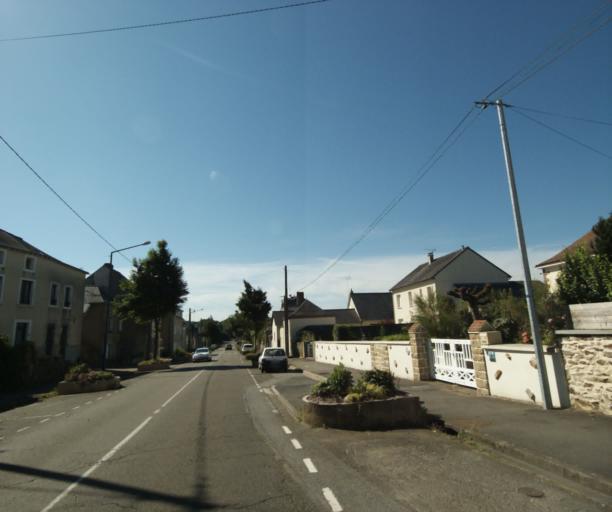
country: FR
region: Pays de la Loire
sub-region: Departement de la Mayenne
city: Laval
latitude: 48.0499
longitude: -0.7464
